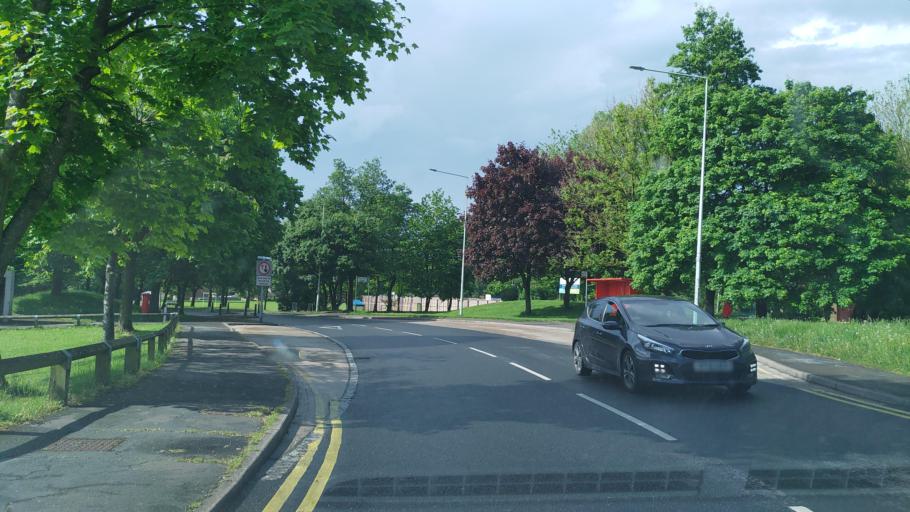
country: GB
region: England
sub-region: Lancashire
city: Clayton-le-Woods
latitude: 53.7121
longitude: -2.6360
